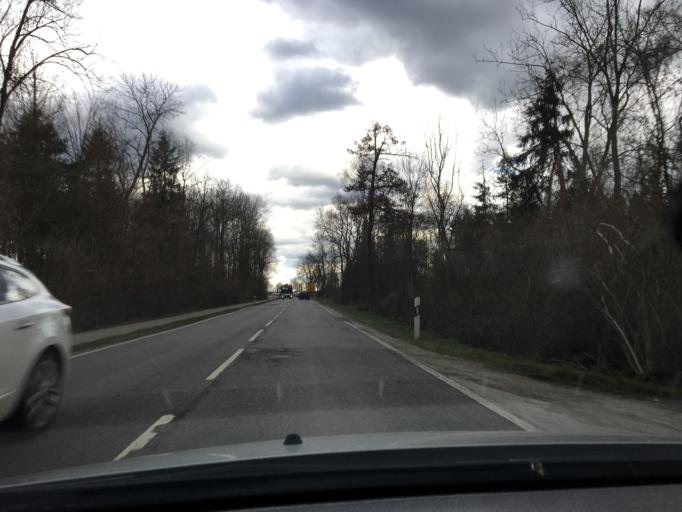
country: DE
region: Bavaria
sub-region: Upper Bavaria
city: Neufahrn bei Freising
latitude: 48.3108
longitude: 11.7061
